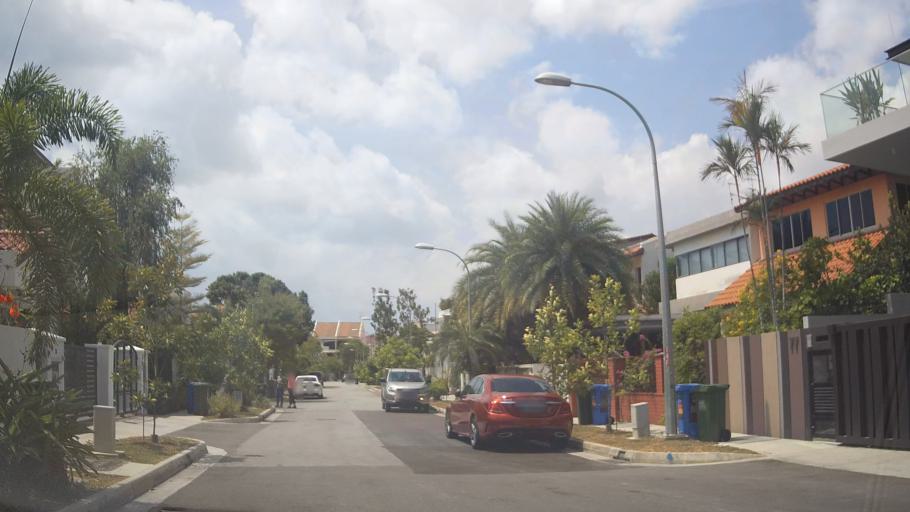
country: SG
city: Singapore
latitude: 1.3245
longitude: 103.9559
